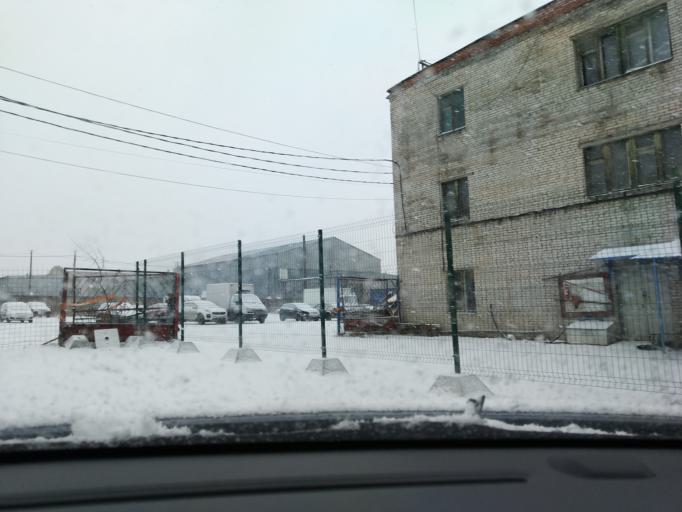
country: RU
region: St.-Petersburg
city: Krasnoye Selo
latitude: 59.7483
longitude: 30.0892
